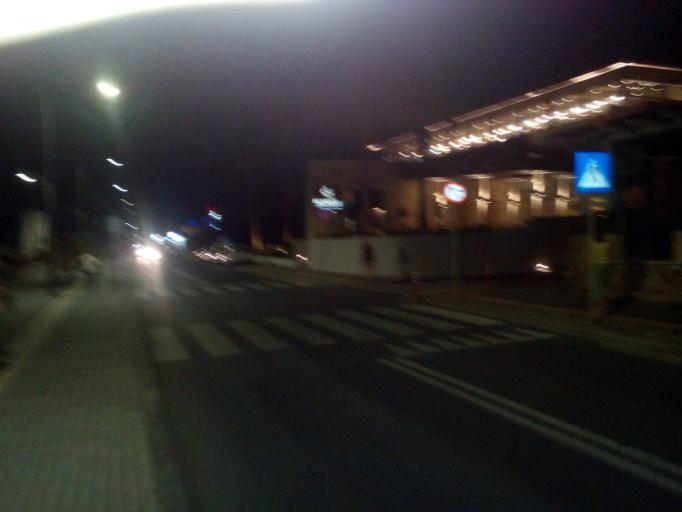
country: GR
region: Crete
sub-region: Nomos Rethymnis
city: Rethymno
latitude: 35.3679
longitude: 24.5023
